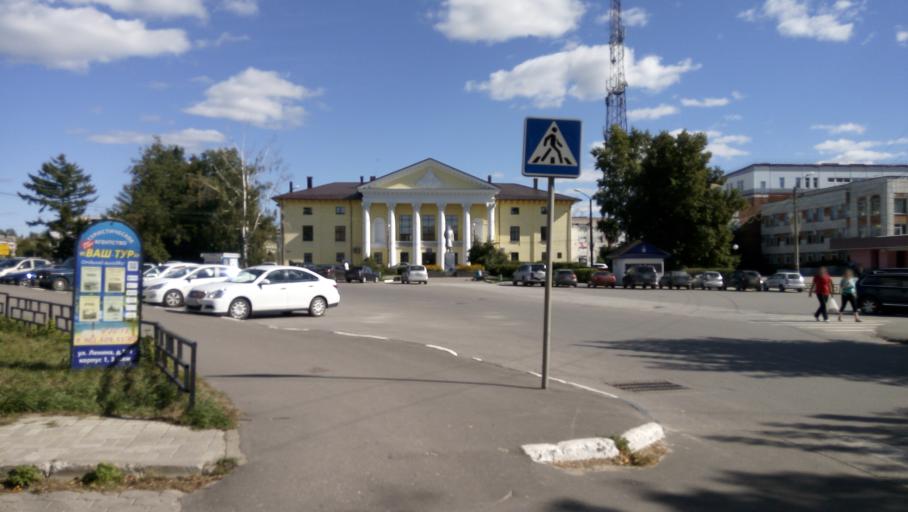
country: RU
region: Nizjnij Novgorod
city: Bor
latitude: 56.3567
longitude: 44.0622
